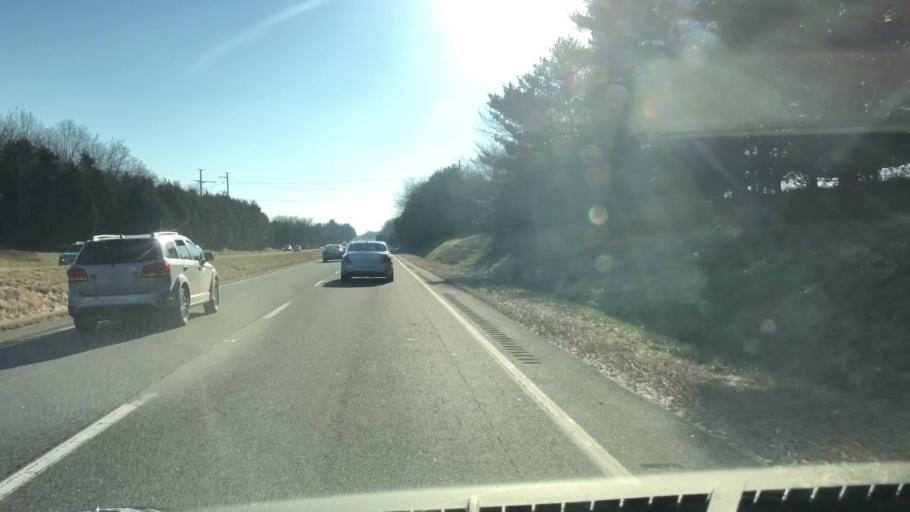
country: US
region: Virginia
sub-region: Fauquier County
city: Bealeton
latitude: 38.5522
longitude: -77.8059
